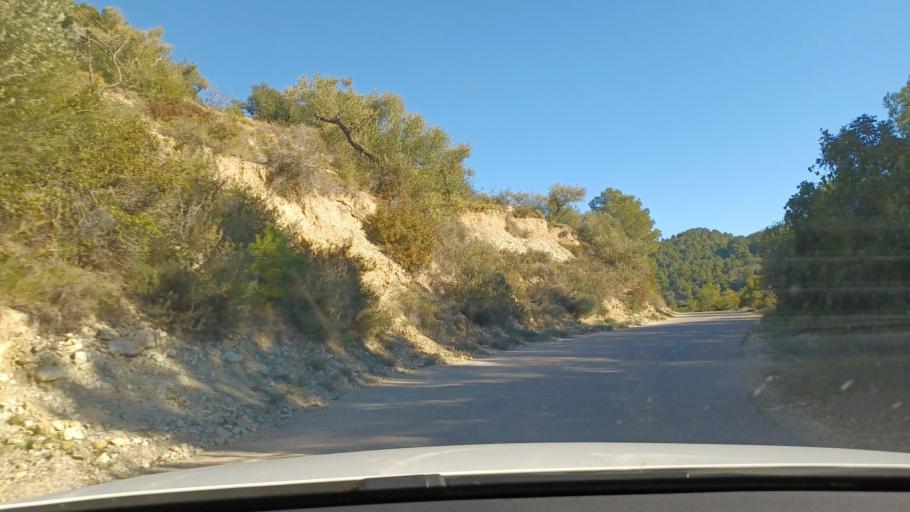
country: ES
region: Catalonia
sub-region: Provincia de Tarragona
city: Tortosa
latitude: 40.8146
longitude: 0.5571
